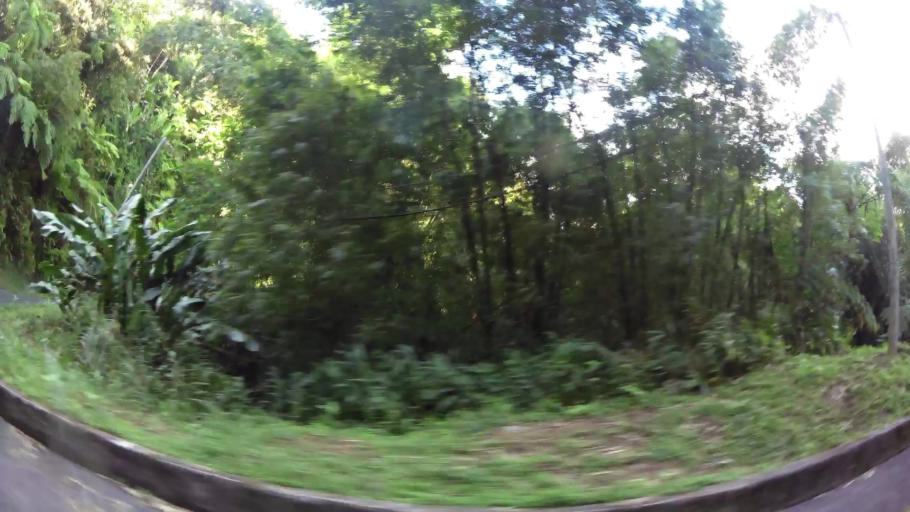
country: MQ
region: Martinique
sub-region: Martinique
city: Saint-Joseph
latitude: 14.6918
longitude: -61.0886
